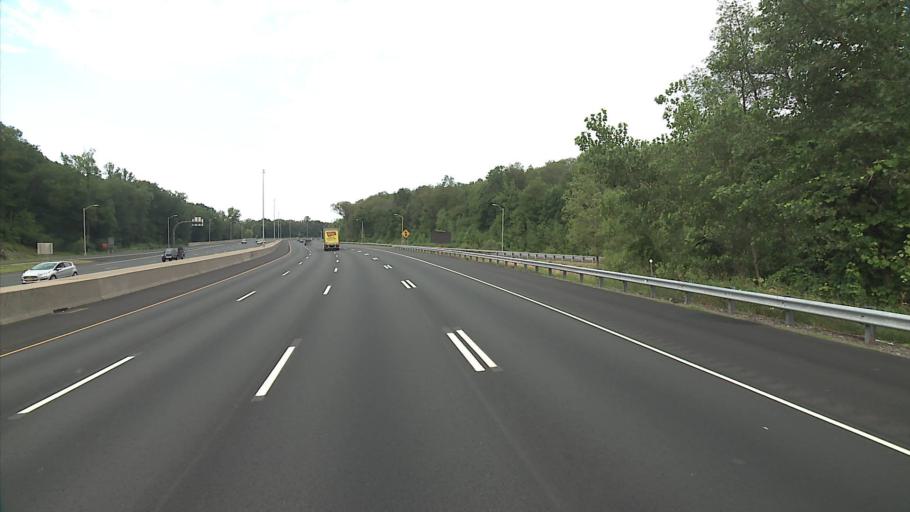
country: US
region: Connecticut
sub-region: New Haven County
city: Prospect
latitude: 41.5404
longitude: -72.9562
